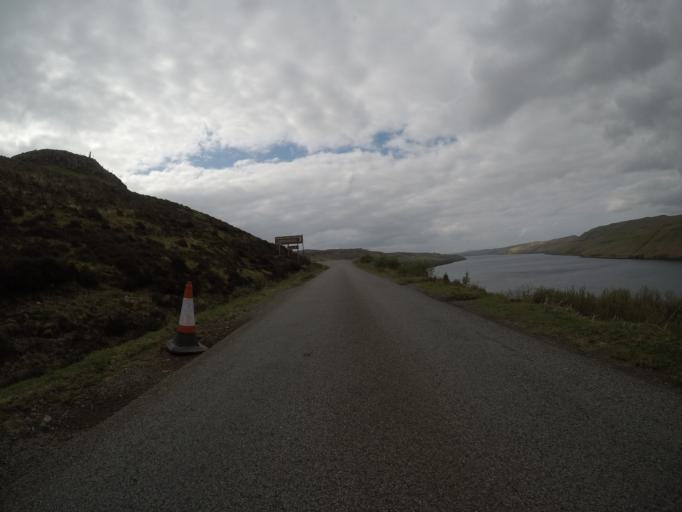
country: GB
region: Scotland
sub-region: Highland
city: Isle of Skye
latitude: 57.2966
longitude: -6.3421
